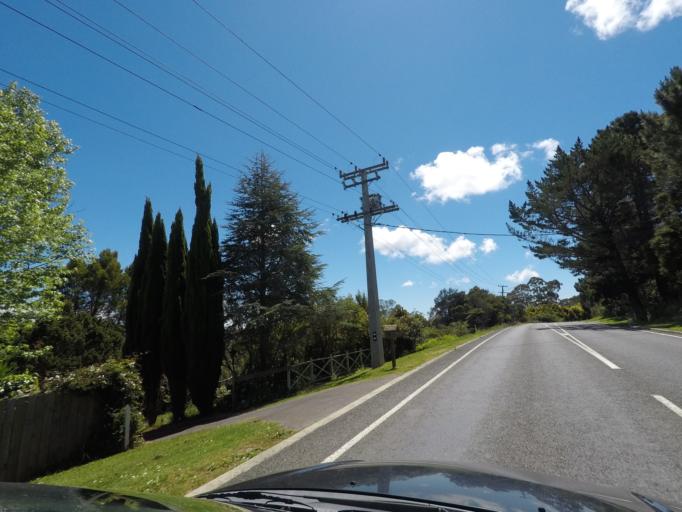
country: NZ
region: Auckland
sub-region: Auckland
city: Rothesay Bay
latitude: -36.7571
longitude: 174.6609
